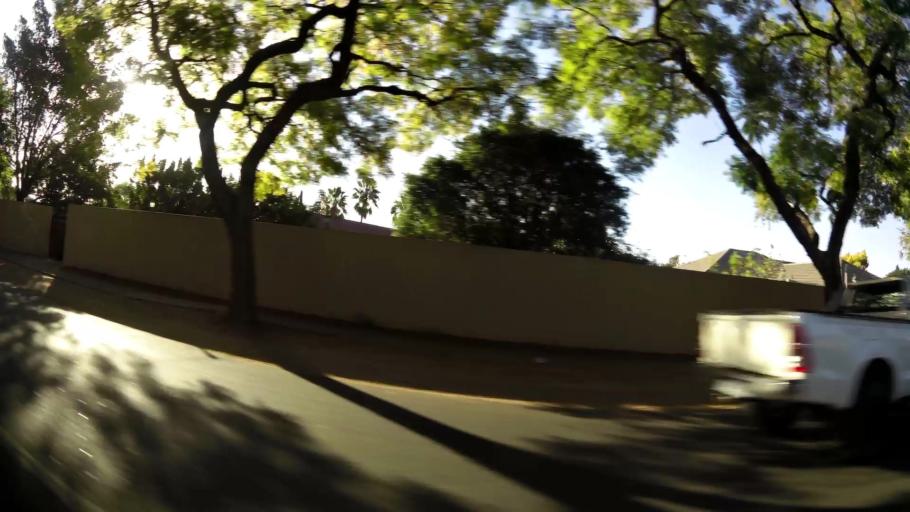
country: ZA
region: Gauteng
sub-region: City of Tshwane Metropolitan Municipality
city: Pretoria
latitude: -25.7220
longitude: 28.2324
